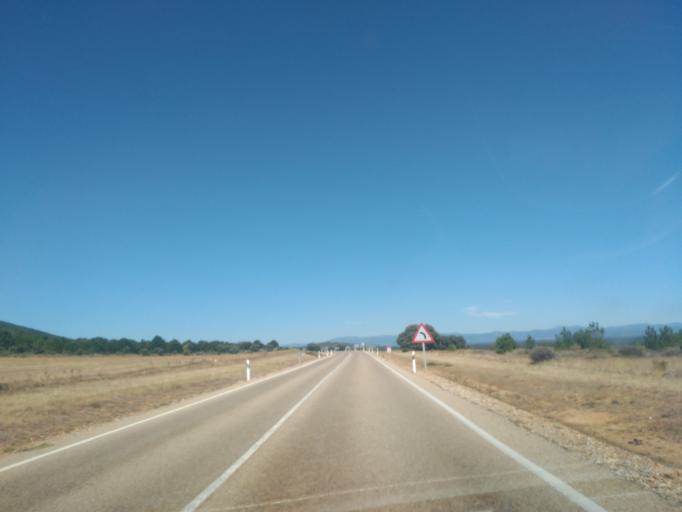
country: ES
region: Castille and Leon
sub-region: Provincia de Zamora
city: Ferreras de Abajo
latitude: 41.9214
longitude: -6.0945
